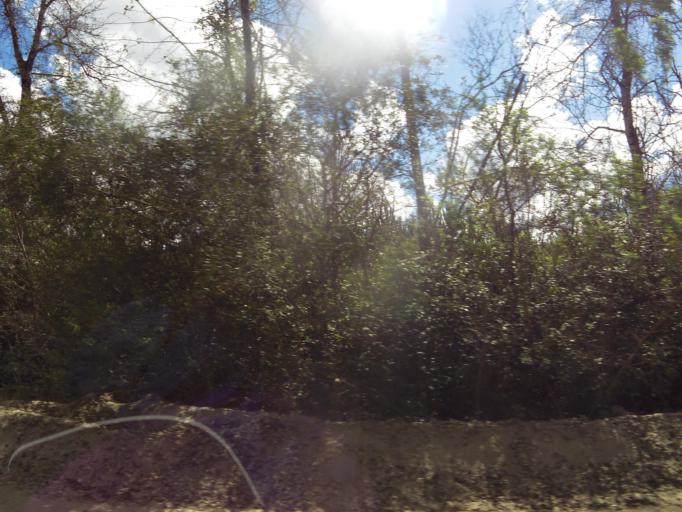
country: US
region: Florida
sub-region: Clay County
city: Green Cove Springs
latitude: 29.8316
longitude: -81.8174
